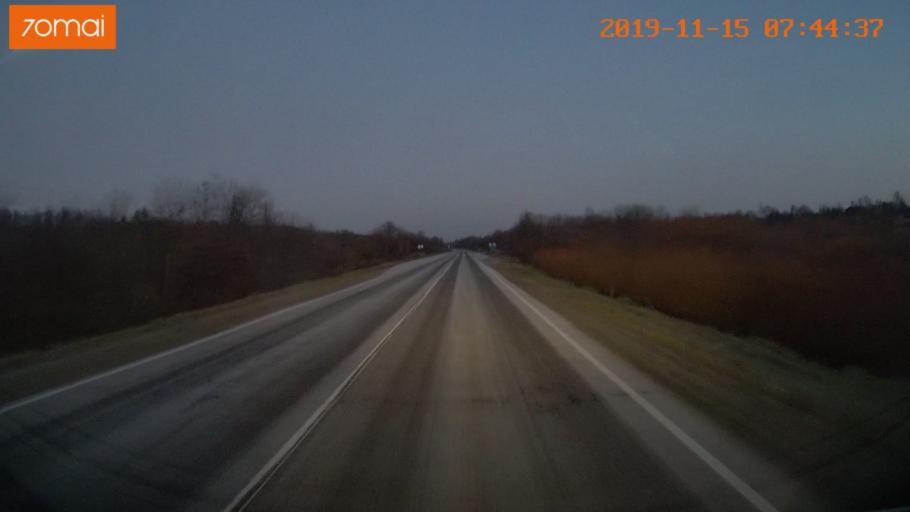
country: RU
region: Vologda
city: Sheksna
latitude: 58.8151
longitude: 38.3107
